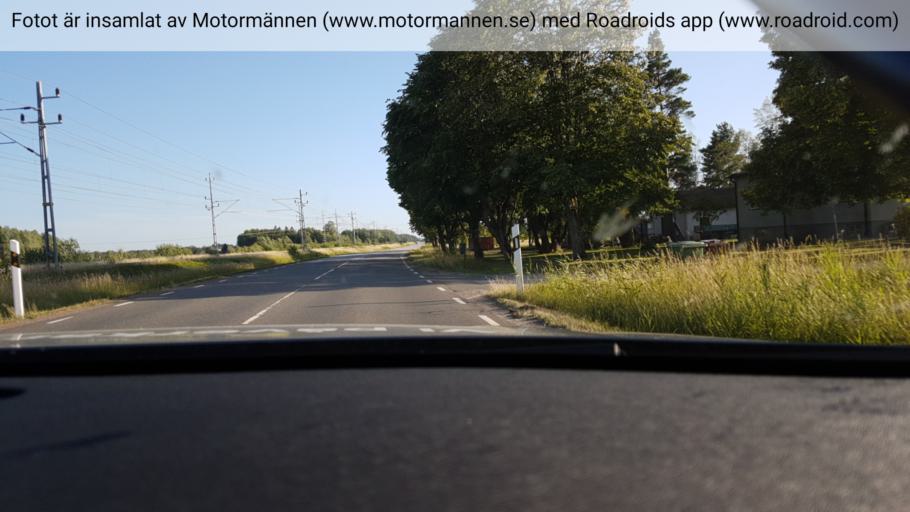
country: SE
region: Vaestra Goetaland
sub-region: Toreboda Kommun
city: Toereboda
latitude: 58.6900
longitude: 14.1141
